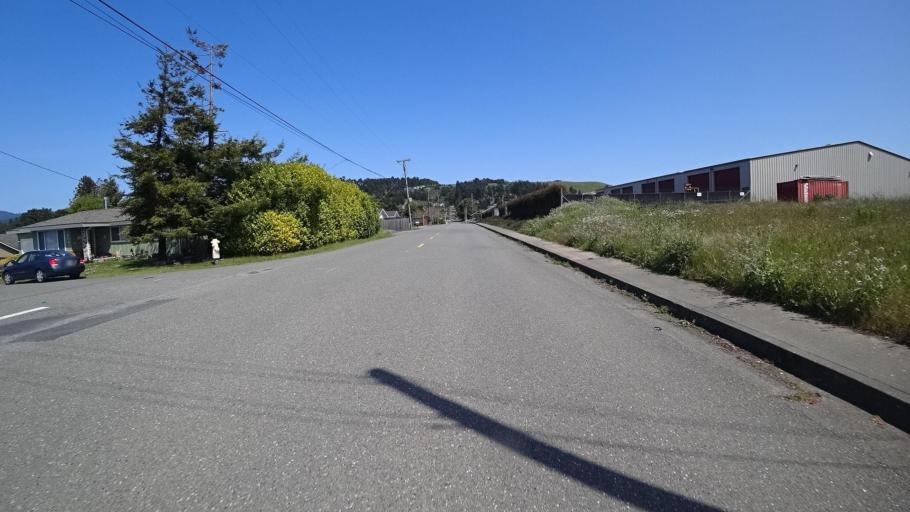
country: US
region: California
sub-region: Humboldt County
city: Hydesville
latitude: 40.5629
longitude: -124.1328
